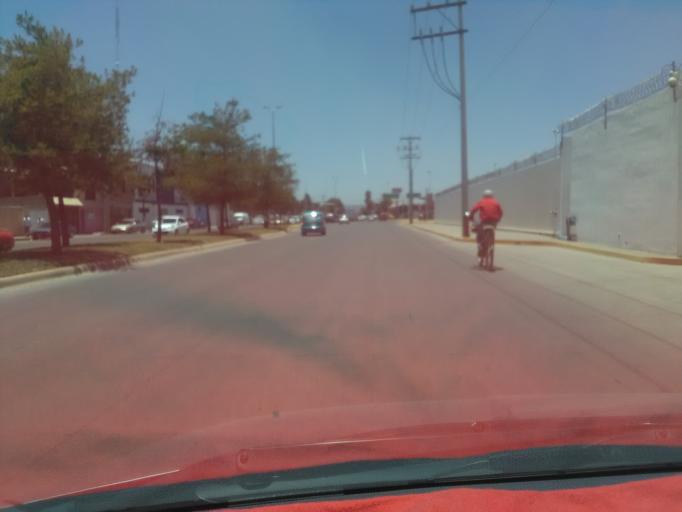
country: MX
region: Durango
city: Victoria de Durango
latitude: 24.0436
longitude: -104.6567
